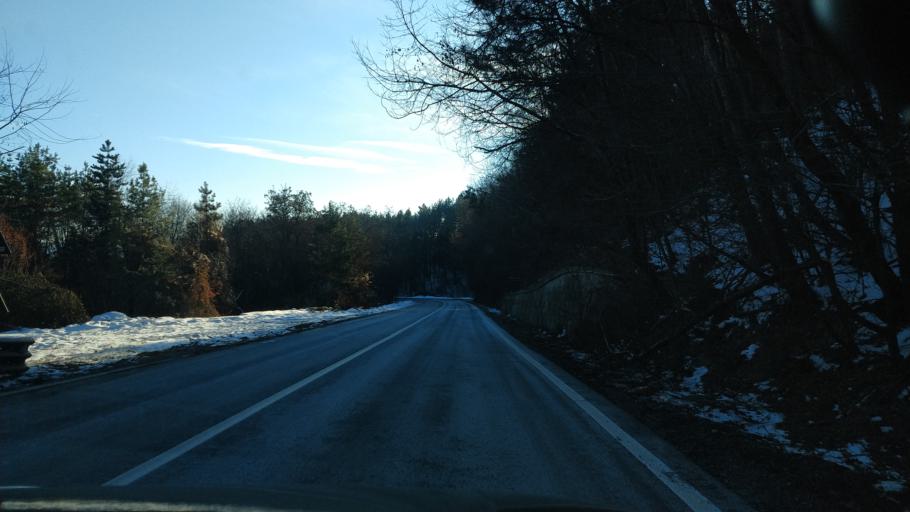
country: RO
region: Bacau
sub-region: Comuna Luizi-Calugara
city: Luizi-Calugara
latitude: 46.5046
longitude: 26.8052
